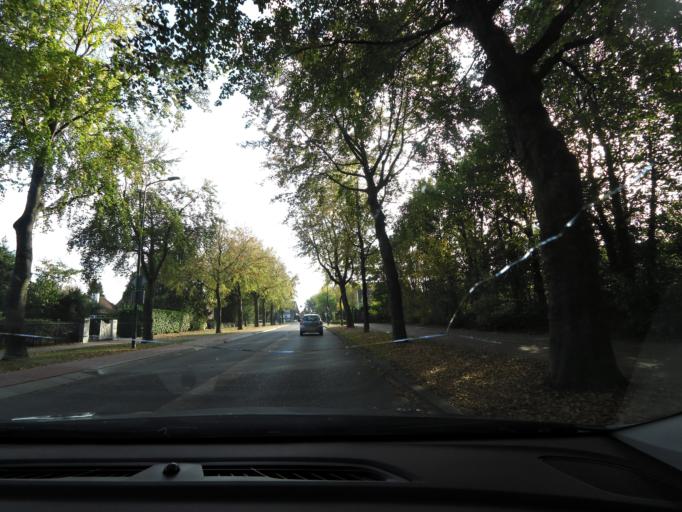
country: NL
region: Utrecht
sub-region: Gemeente Rhenen
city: Rhenen
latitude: 51.9667
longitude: 5.5663
